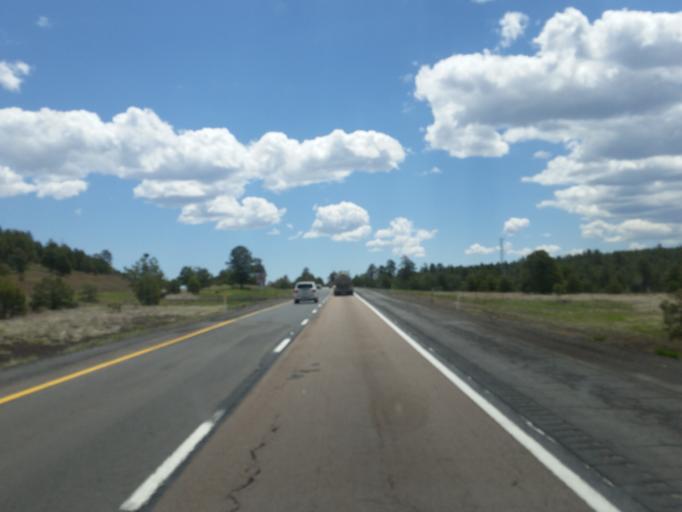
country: US
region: Arizona
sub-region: Coconino County
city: Flagstaff
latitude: 35.2001
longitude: -111.7569
